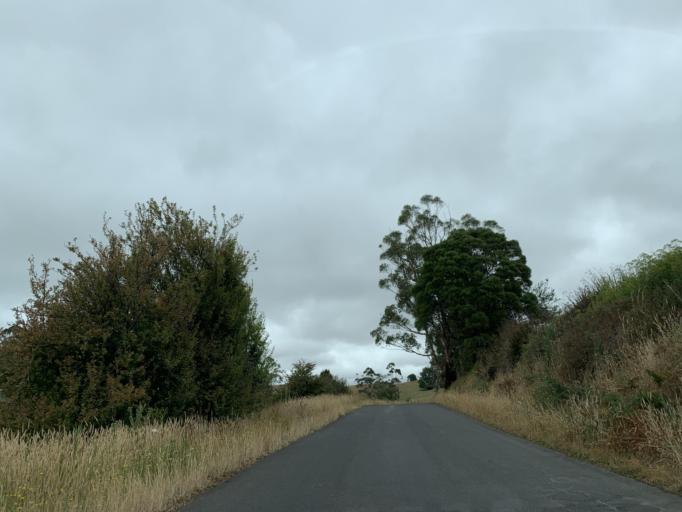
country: AU
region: Victoria
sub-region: Baw Baw
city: Warragul
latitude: -38.2909
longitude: 145.8322
